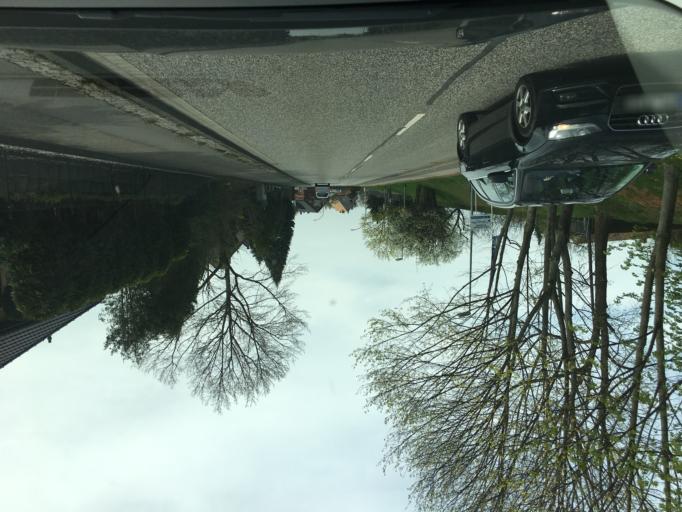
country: DE
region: Brandenburg
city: Spremberg
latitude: 51.5677
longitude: 14.3938
